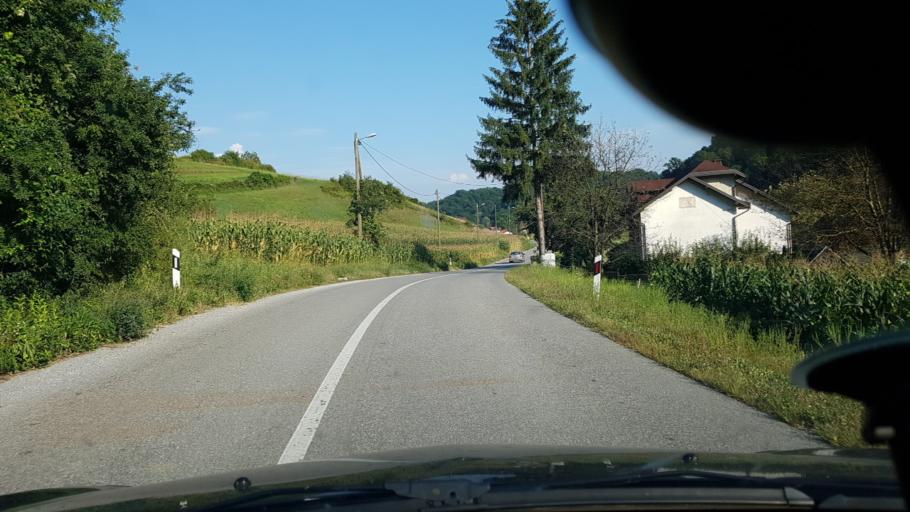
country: SI
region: Bistrica ob Sotli
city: Bistrica ob Sotli
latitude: 46.0380
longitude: 15.7657
